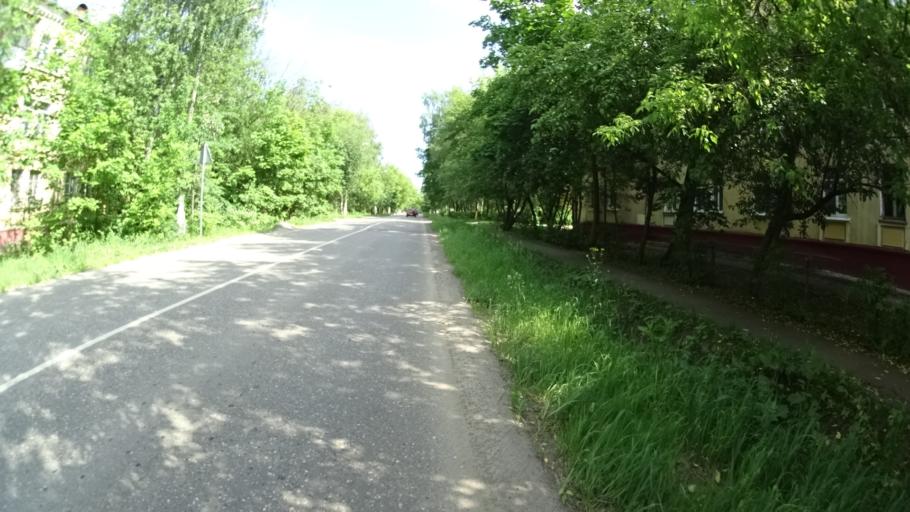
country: RU
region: Moskovskaya
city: Lesnoy
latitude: 56.0790
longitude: 37.9275
